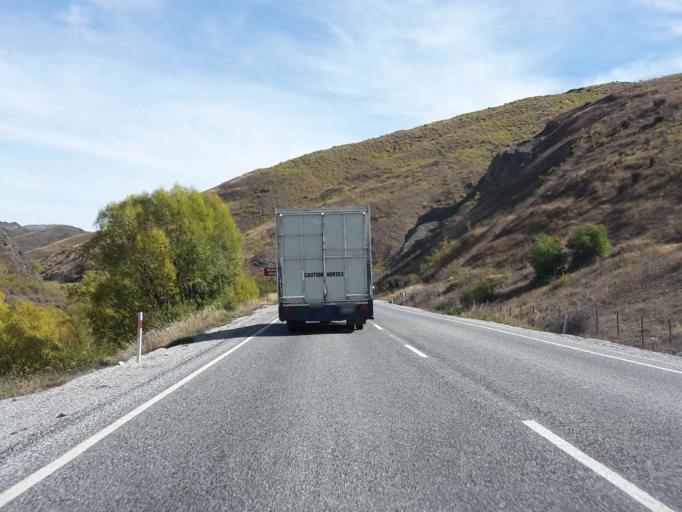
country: NZ
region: Otago
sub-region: Queenstown-Lakes District
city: Wanaka
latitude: -44.6954
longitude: 169.4891
